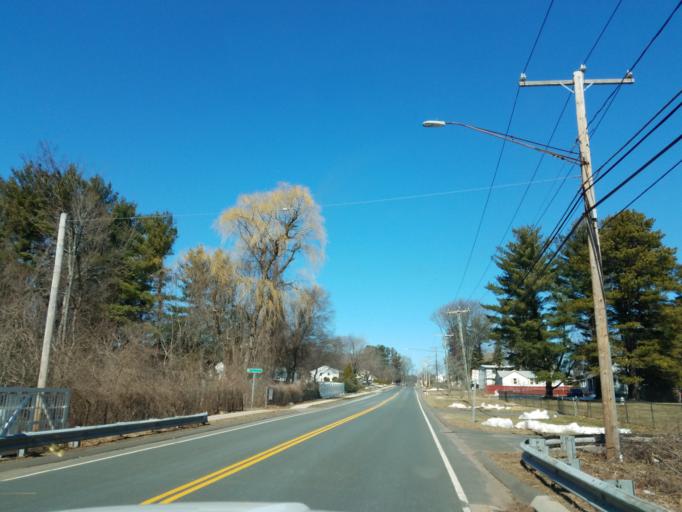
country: US
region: Connecticut
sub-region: Hartford County
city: Windsor Locks
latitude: 41.9066
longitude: -72.6358
